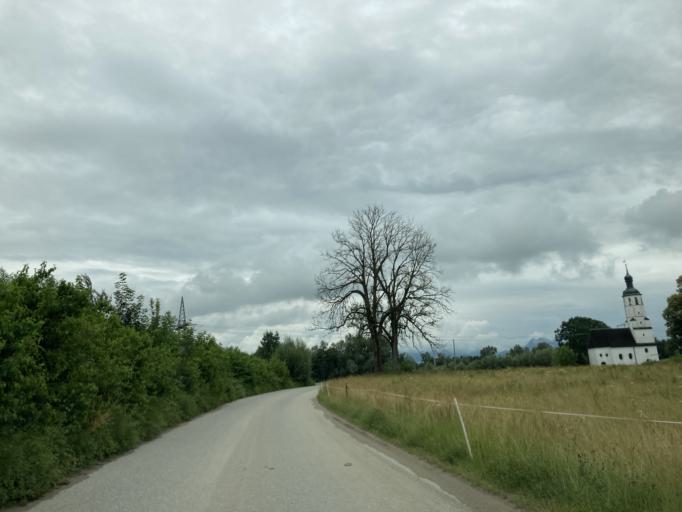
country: DE
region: Bavaria
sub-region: Upper Bavaria
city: Stephanskirchen
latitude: 47.8708
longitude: 12.1650
